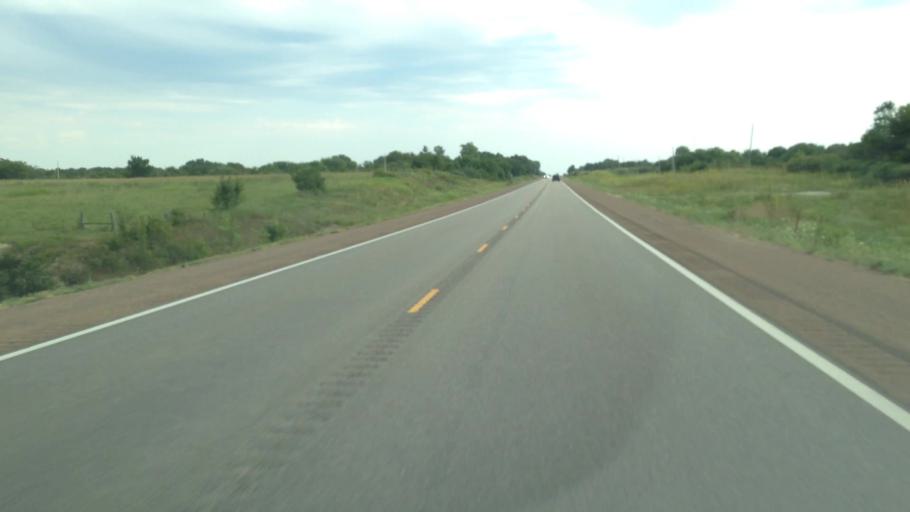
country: US
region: Kansas
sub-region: Woodson County
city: Yates Center
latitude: 37.9984
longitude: -95.7389
